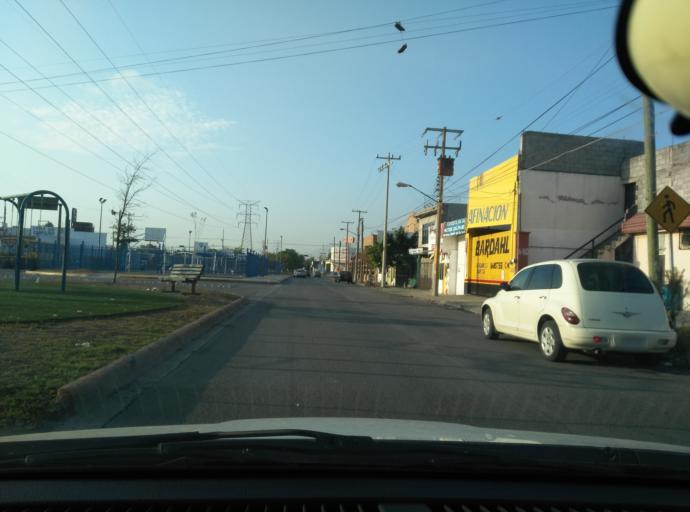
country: MX
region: Nuevo Leon
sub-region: San Nicolas de los Garza
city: San Nicolas de los Garza
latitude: 25.7559
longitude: -100.2481
